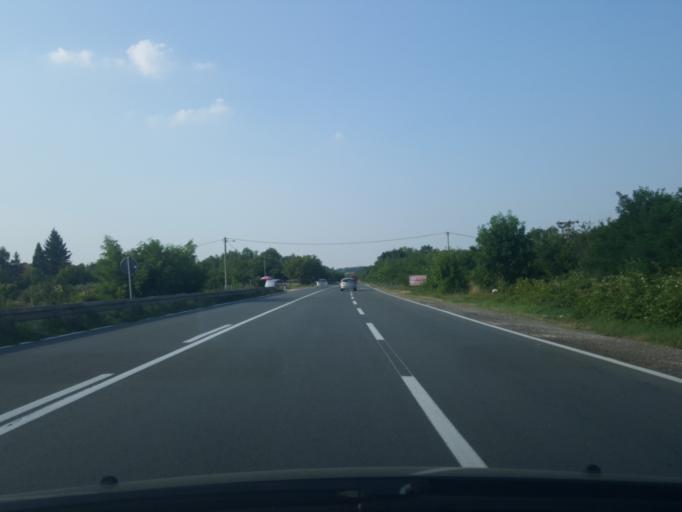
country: RS
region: Central Serbia
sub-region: Belgrade
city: Sopot
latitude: 44.5188
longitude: 20.6531
